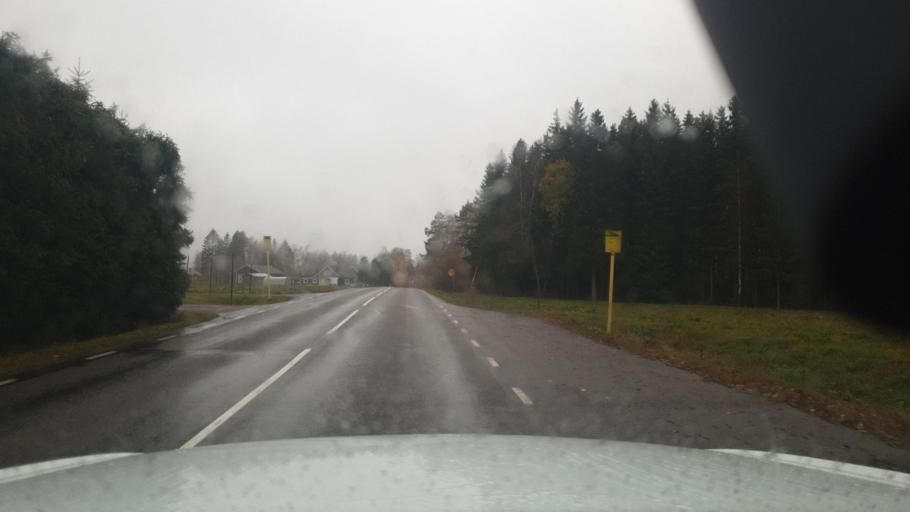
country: SE
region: Vaermland
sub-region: Sunne Kommun
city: Sunne
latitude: 59.7923
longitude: 13.0769
